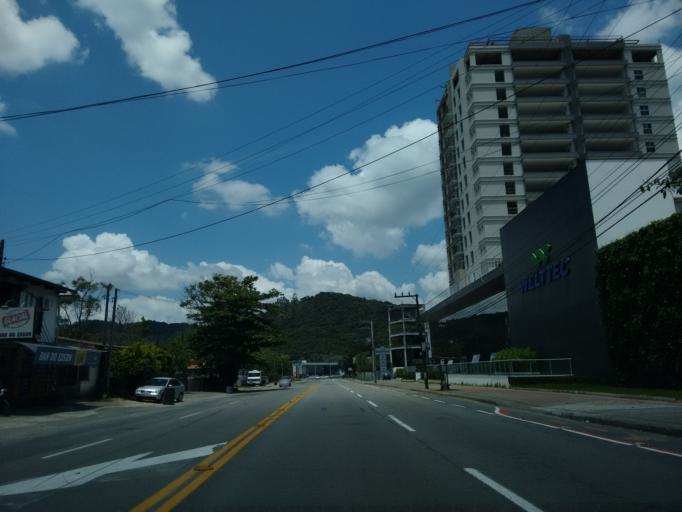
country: BR
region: Santa Catarina
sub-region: Blumenau
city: Blumenau
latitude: -26.9033
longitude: -49.0350
